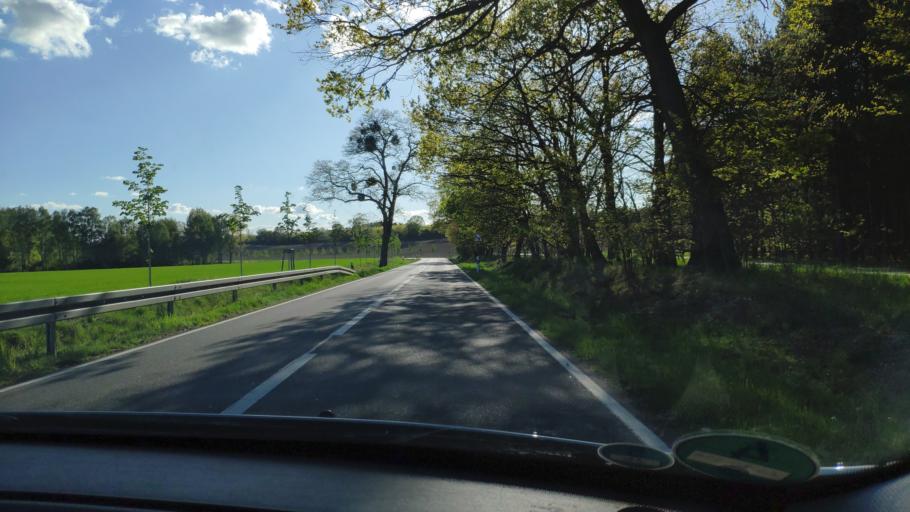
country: DE
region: Mecklenburg-Vorpommern
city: Wesenberg
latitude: 53.3459
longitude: 12.9922
